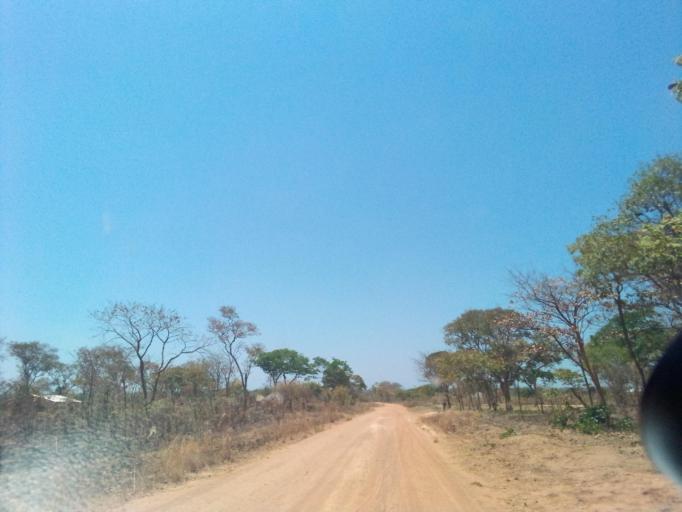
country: ZM
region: Northern
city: Mpika
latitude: -12.2517
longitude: 30.6743
